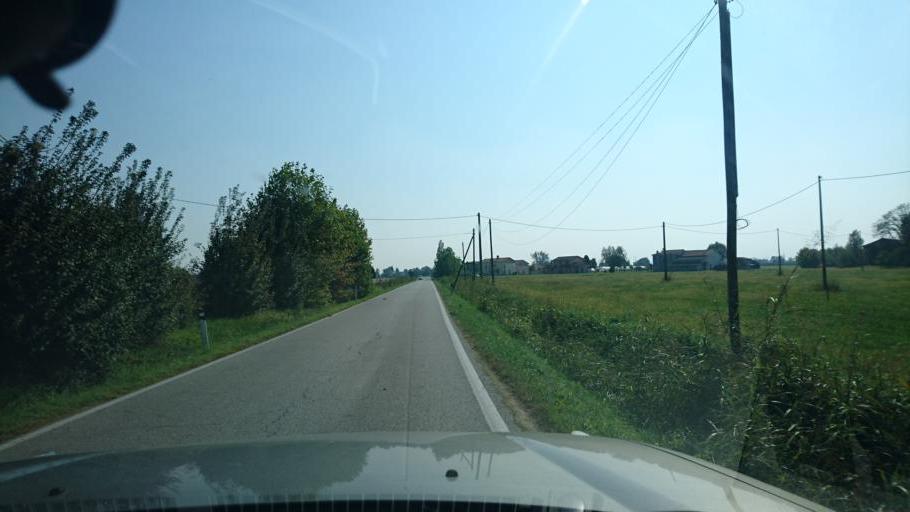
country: IT
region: Veneto
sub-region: Provincia di Vicenza
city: Camisano Vicentino
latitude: 45.5477
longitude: 11.7129
